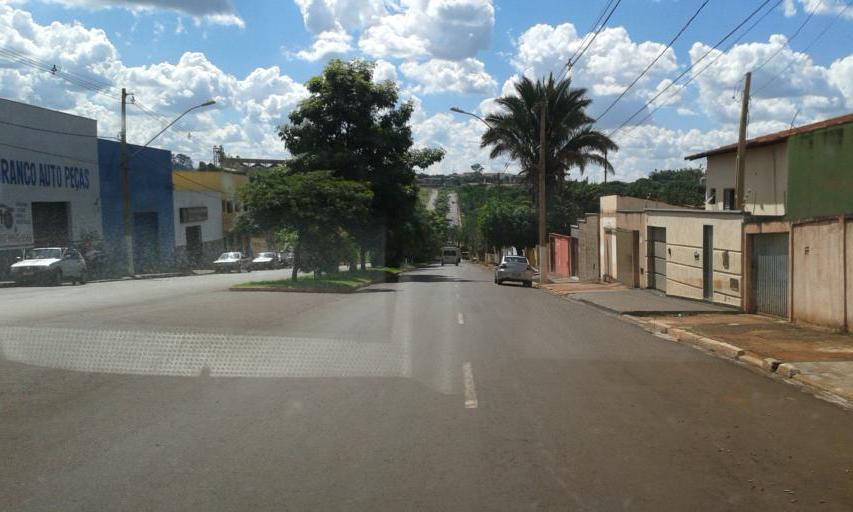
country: BR
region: Minas Gerais
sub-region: Ituiutaba
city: Ituiutaba
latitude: -18.9715
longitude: -49.4865
